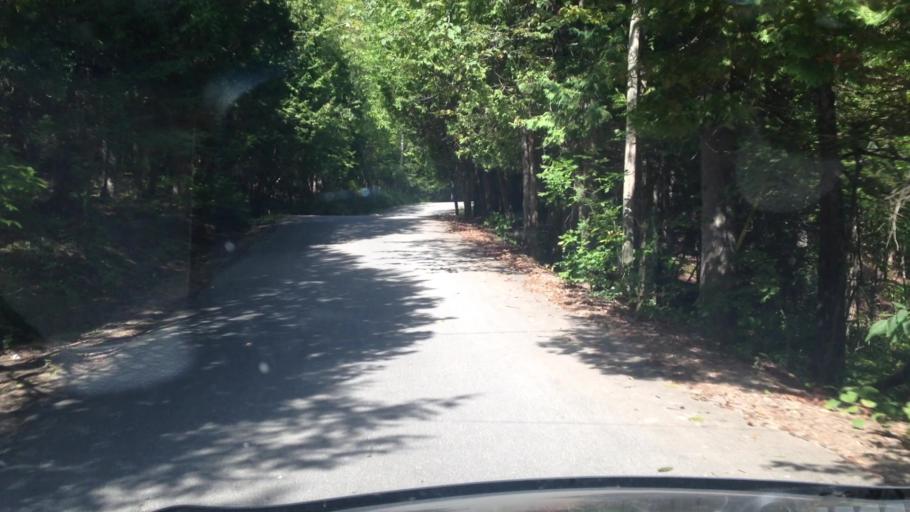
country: CA
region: Quebec
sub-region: Laurentides
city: Mont-Tremblant
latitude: 45.9402
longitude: -74.5862
